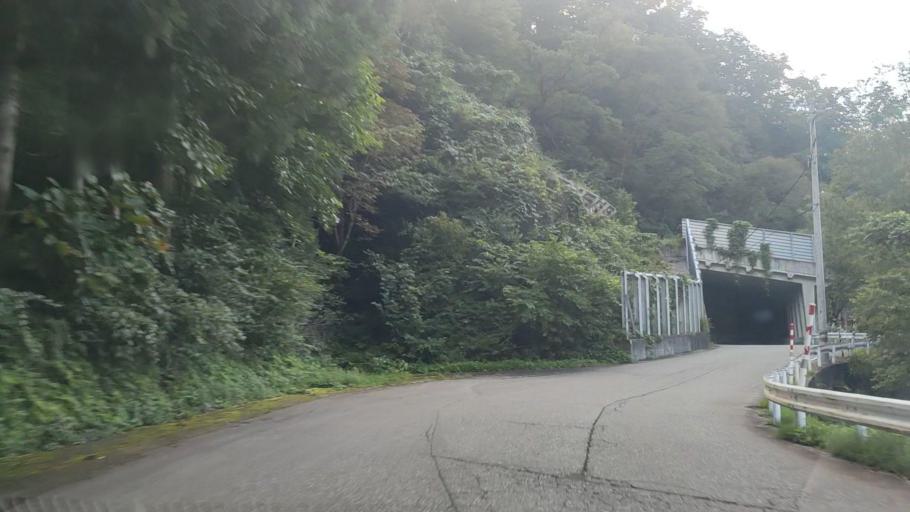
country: JP
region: Toyama
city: Yatsuomachi-higashikumisaka
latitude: 36.4838
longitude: 137.0675
